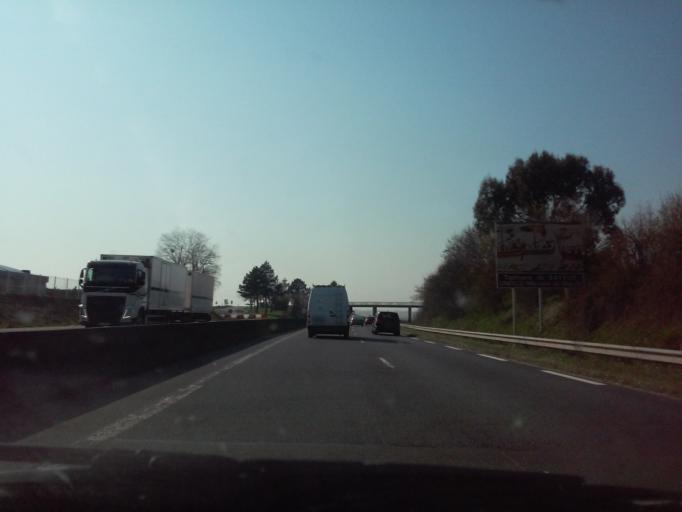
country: FR
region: Lower Normandy
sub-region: Departement du Calvados
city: Tilly-sur-Seulles
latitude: 49.2397
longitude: -0.5994
